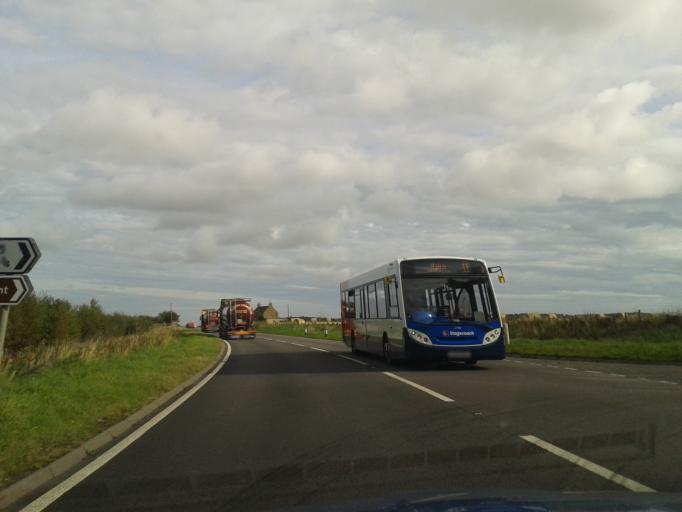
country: GB
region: Scotland
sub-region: Moray
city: Kinloss
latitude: 57.6264
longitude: -3.5189
